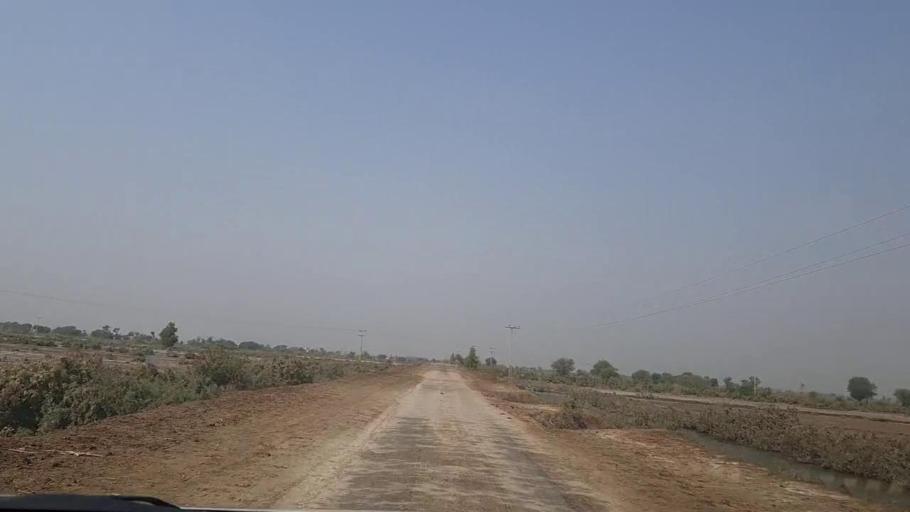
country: PK
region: Sindh
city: Pithoro
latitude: 25.5705
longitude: 69.2049
